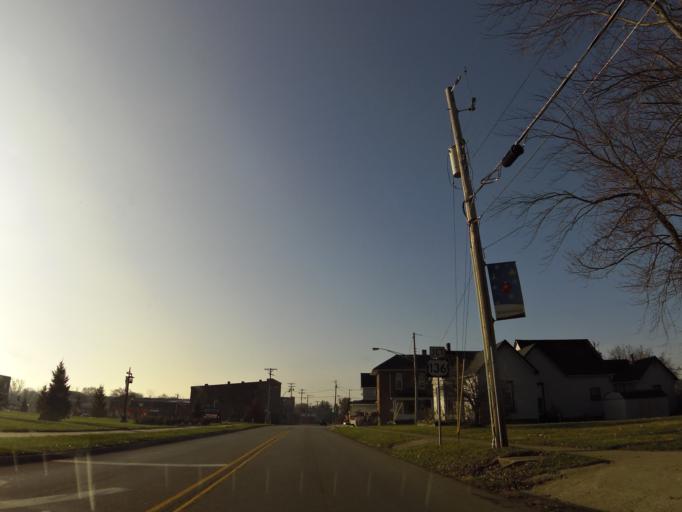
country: US
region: Indiana
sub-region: Hendricks County
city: Brownsburg
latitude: 39.8451
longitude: -86.3972
